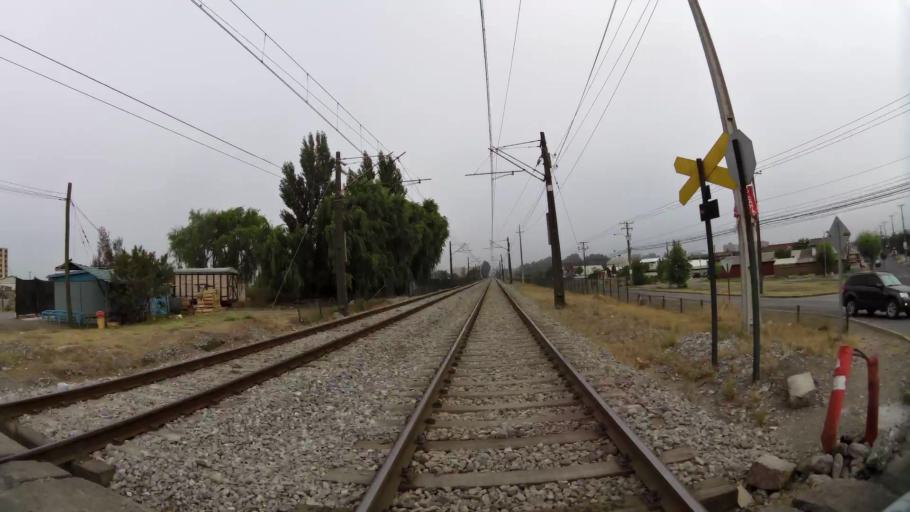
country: CL
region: Biobio
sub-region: Provincia de Concepcion
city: Concepcion
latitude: -36.7961
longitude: -73.0823
